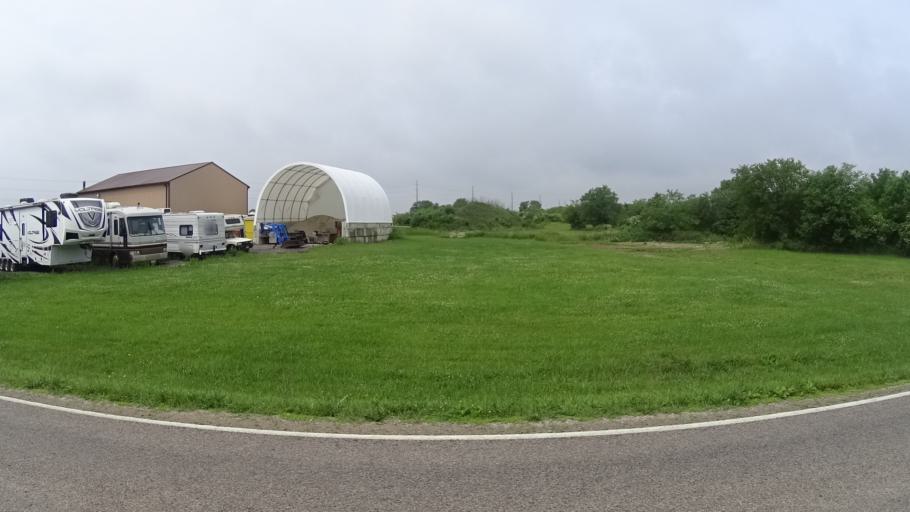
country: US
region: Ohio
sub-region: Erie County
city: Sandusky
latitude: 41.3559
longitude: -82.7559
